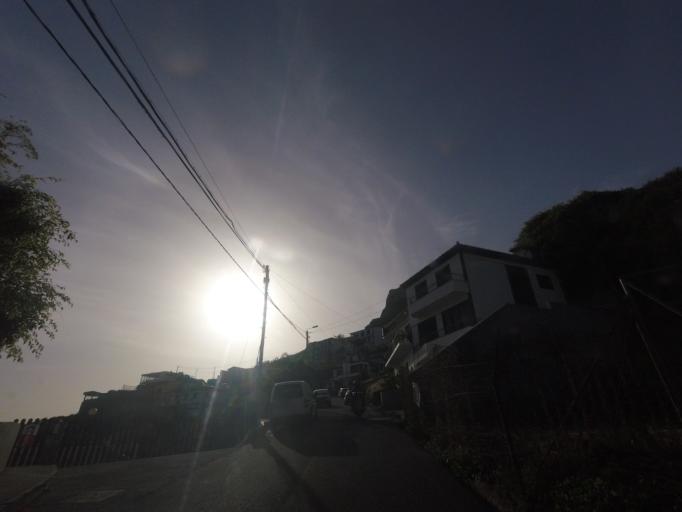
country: PT
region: Madeira
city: Camara de Lobos
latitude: 32.6534
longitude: -16.9908
